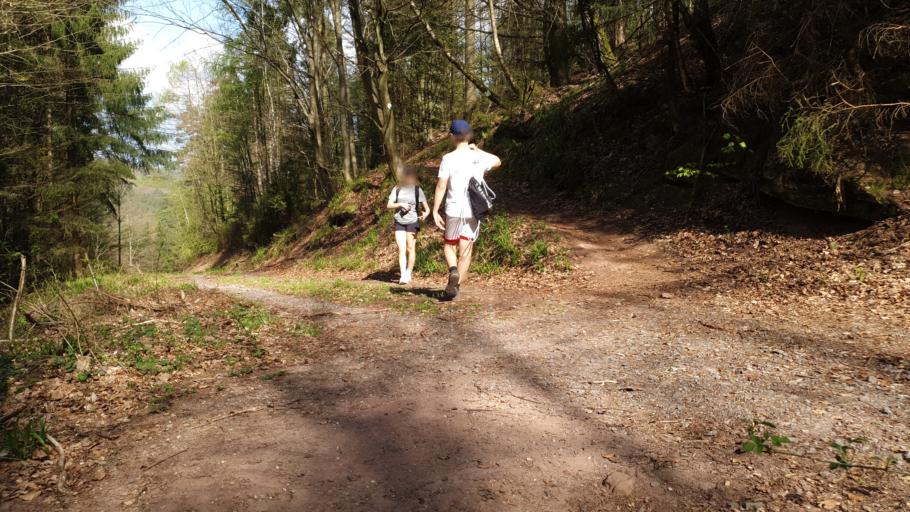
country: DE
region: Rheinland-Pfalz
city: Rodalben
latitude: 49.2280
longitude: 7.6220
